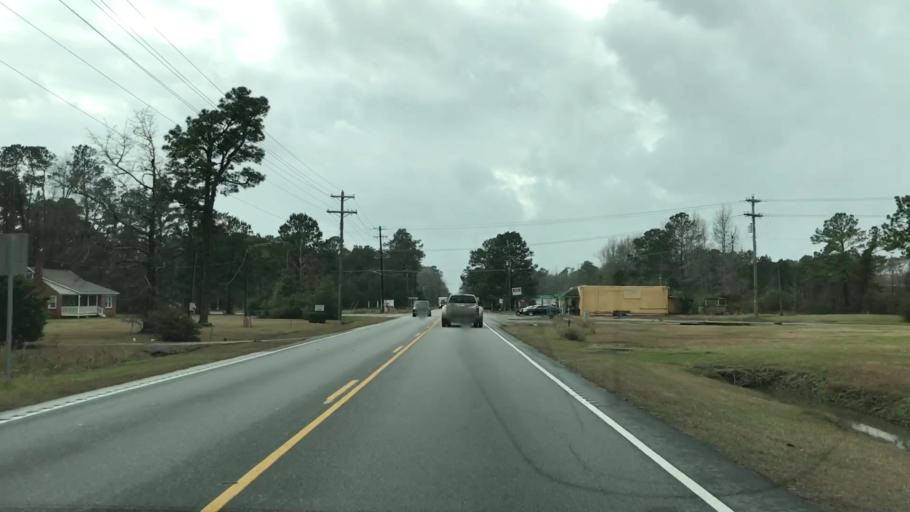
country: US
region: South Carolina
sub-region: Horry County
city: Socastee
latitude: 33.6918
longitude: -79.1169
